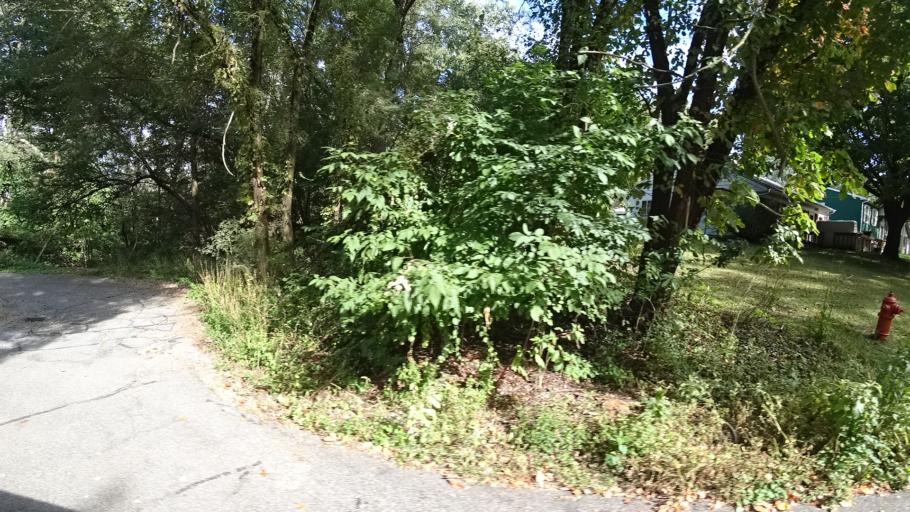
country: US
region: Indiana
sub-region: LaPorte County
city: Michigan City
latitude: 41.7206
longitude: -86.8760
